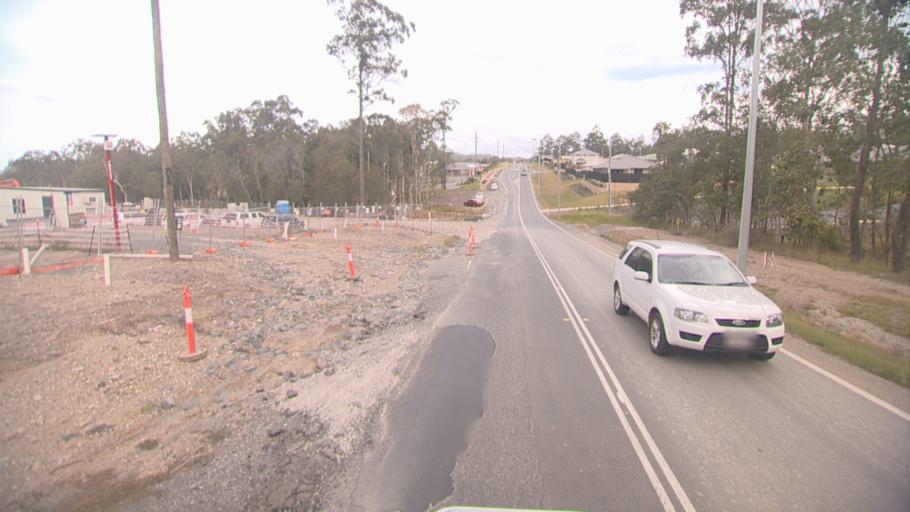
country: AU
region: Queensland
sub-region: Logan
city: Windaroo
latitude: -27.7273
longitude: 153.1638
